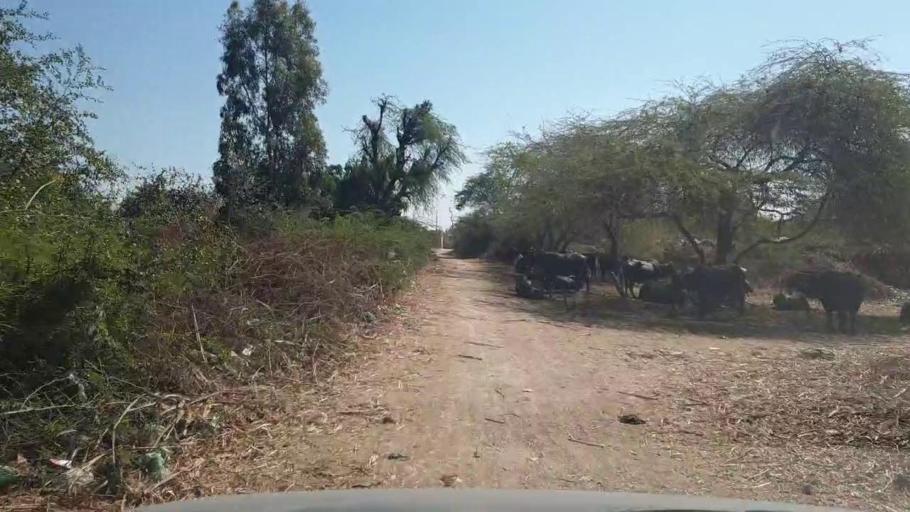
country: PK
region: Sindh
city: Mirwah Gorchani
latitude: 25.2909
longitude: 69.1257
